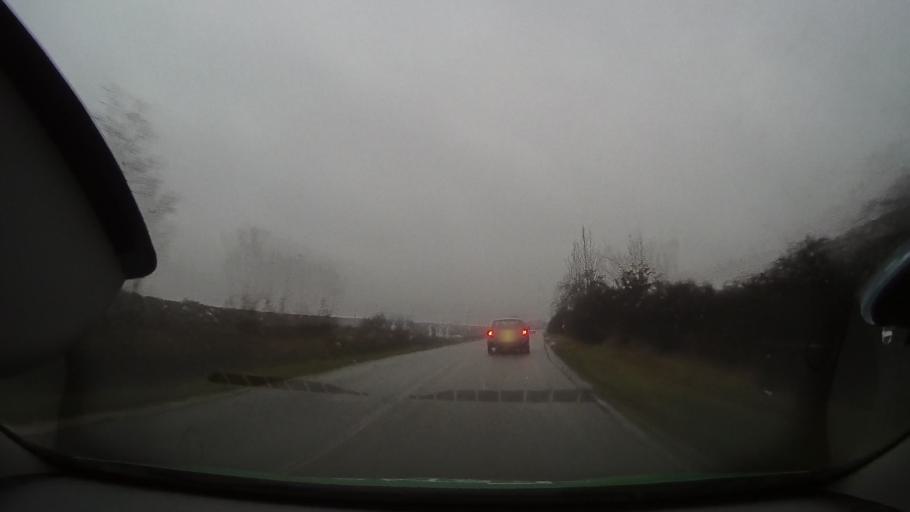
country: RO
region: Arad
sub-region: Comuna Craiova
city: Craiova
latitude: 46.5920
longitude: 21.9783
